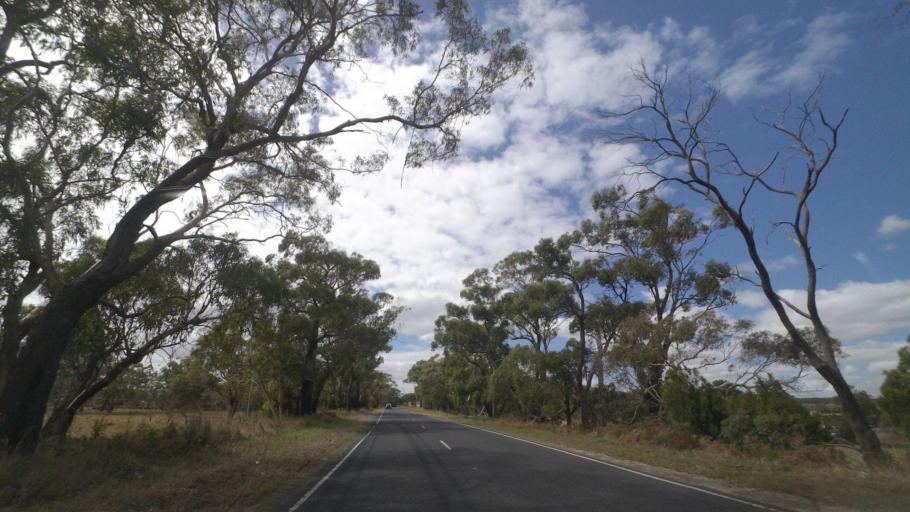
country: AU
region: Victoria
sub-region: Cardinia
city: Koo-Wee-Rup
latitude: -38.2847
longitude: 145.6098
